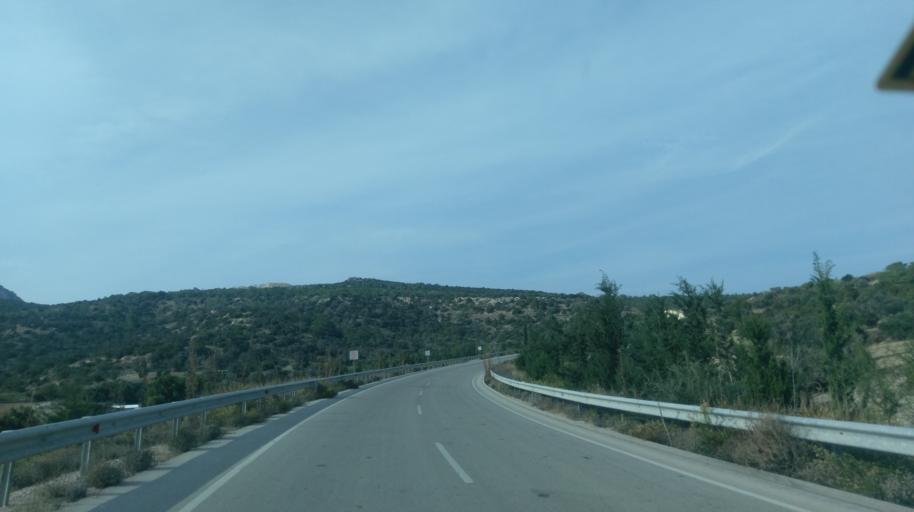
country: CY
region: Ammochostos
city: Trikomo
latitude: 35.4182
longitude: 33.9815
